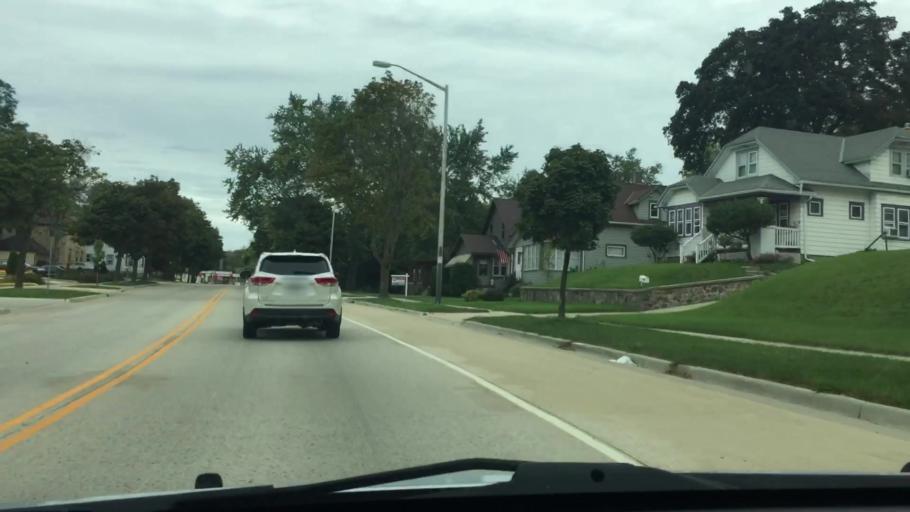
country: US
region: Wisconsin
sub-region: Waukesha County
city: Waukesha
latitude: 43.0163
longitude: -88.2360
